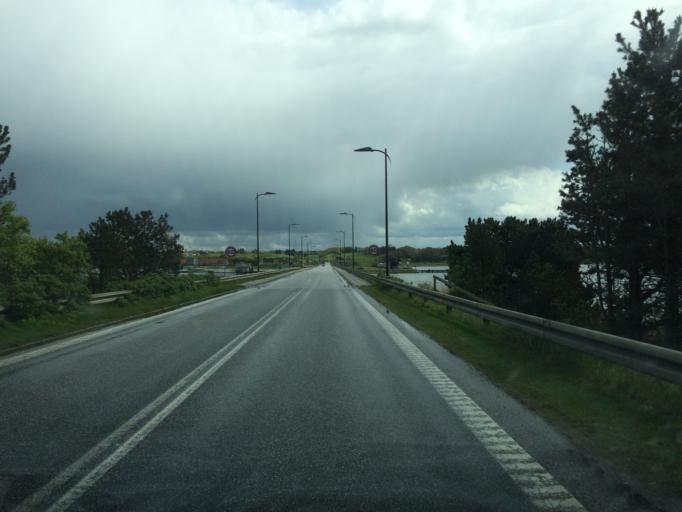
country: DK
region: Central Jutland
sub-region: Skive Kommune
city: Hojslev
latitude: 56.6065
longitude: 9.2877
